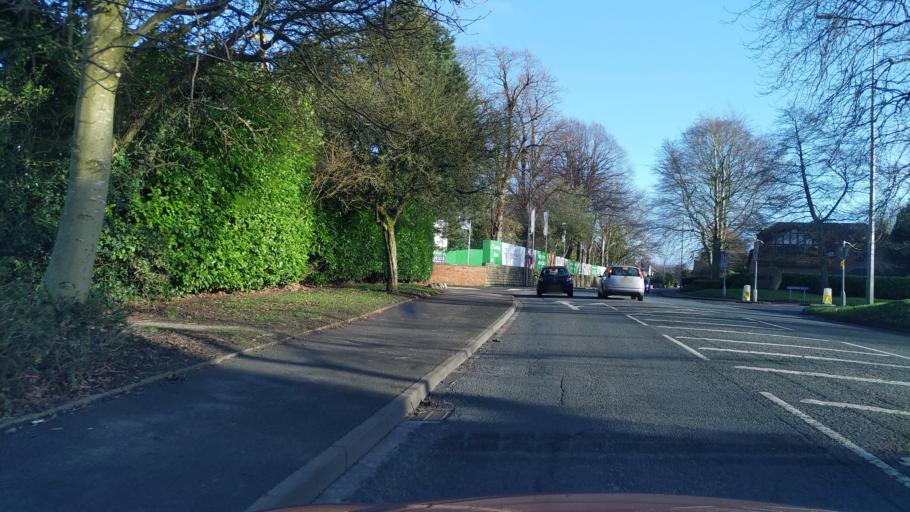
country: GB
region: England
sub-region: Lancashire
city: Leyland
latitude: 53.6890
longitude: -2.6907
